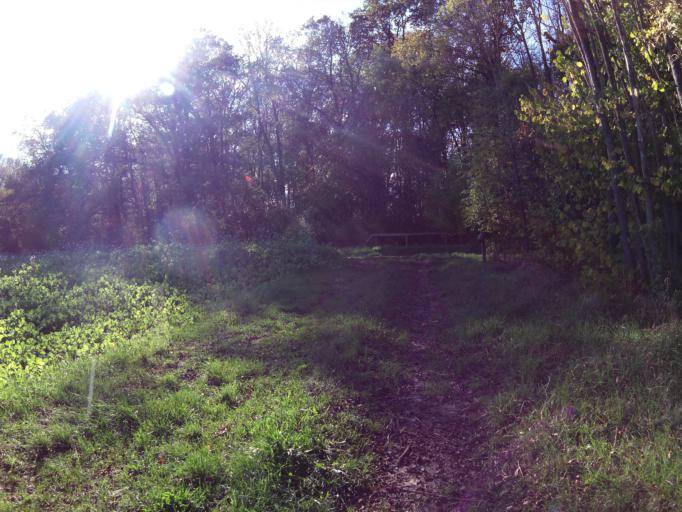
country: DE
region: Bavaria
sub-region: Regierungsbezirk Unterfranken
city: Biebelried
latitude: 49.7238
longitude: 10.0880
